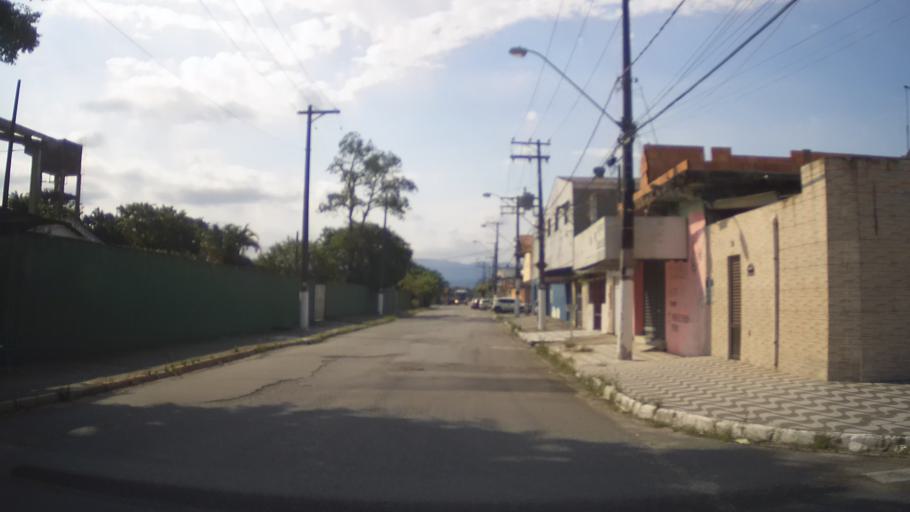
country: BR
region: Sao Paulo
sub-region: Praia Grande
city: Praia Grande
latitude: -24.0012
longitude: -46.4290
